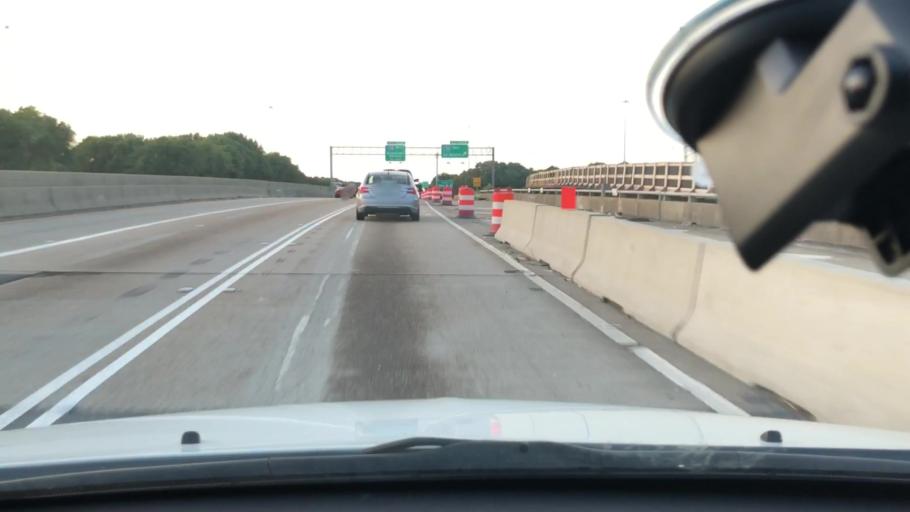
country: US
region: Virginia
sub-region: City of Chesapeake
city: Chesapeake
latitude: 36.8407
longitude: -76.1965
